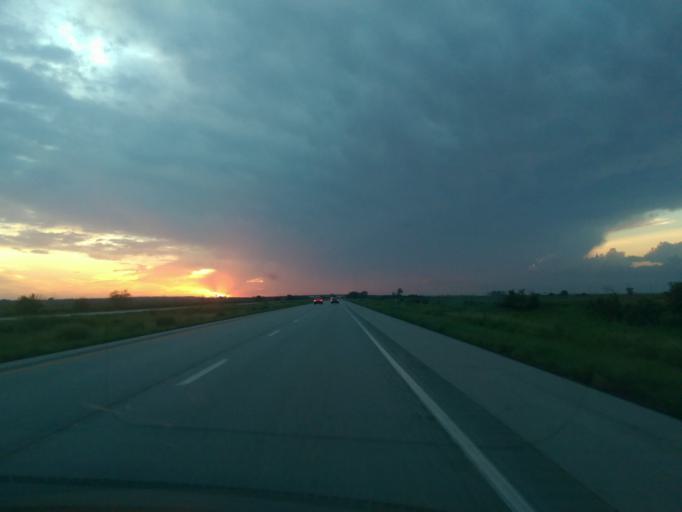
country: US
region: Iowa
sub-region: Fremont County
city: Hamburg
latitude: 40.6339
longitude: -95.7248
